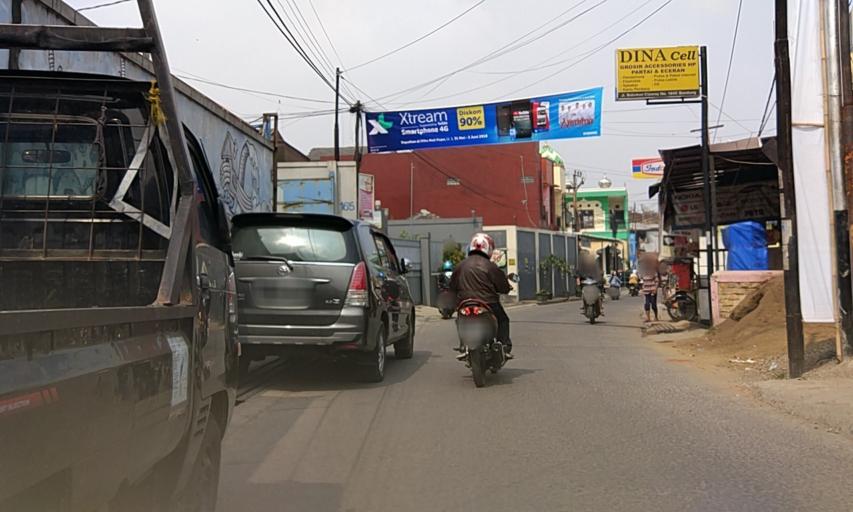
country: ID
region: West Java
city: Margahayukencana
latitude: -6.9356
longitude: 107.5846
